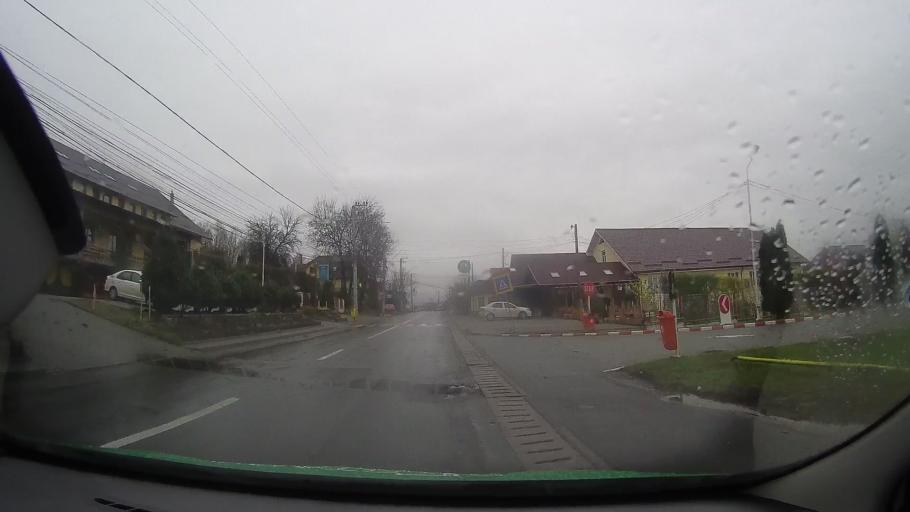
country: RO
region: Mures
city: Reghin-Sat
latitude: 46.7916
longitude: 24.7140
